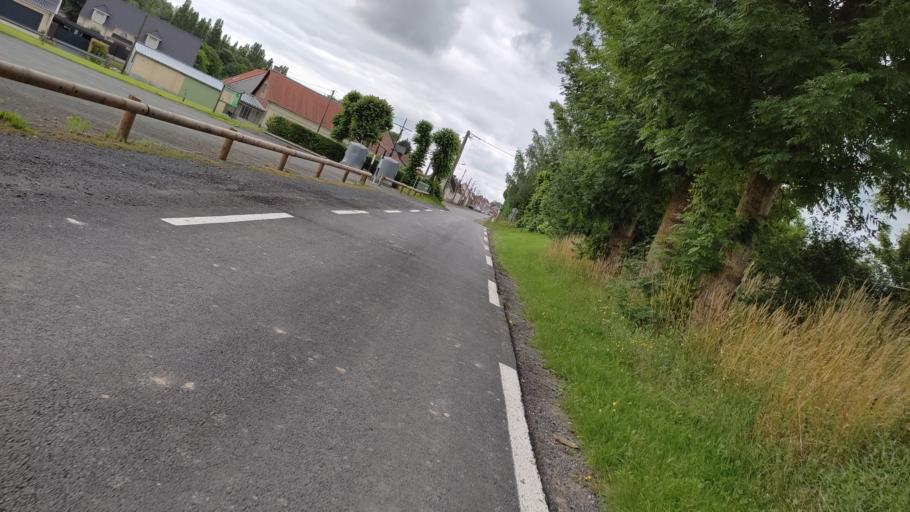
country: FR
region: Nord-Pas-de-Calais
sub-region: Departement du Pas-de-Calais
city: Beaumetz-les-Loges
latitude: 50.2670
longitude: 2.6785
